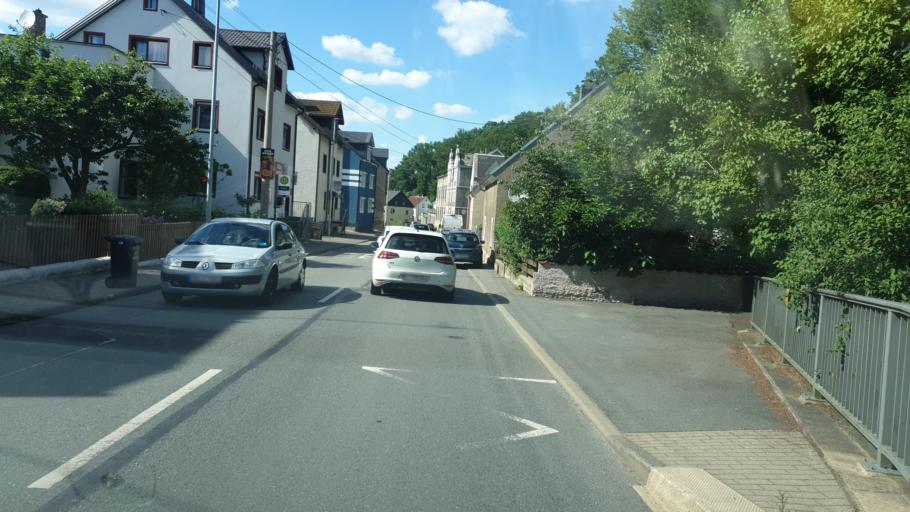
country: DE
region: Saxony
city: Burkhardtsdorf
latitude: 50.7656
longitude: 12.9064
